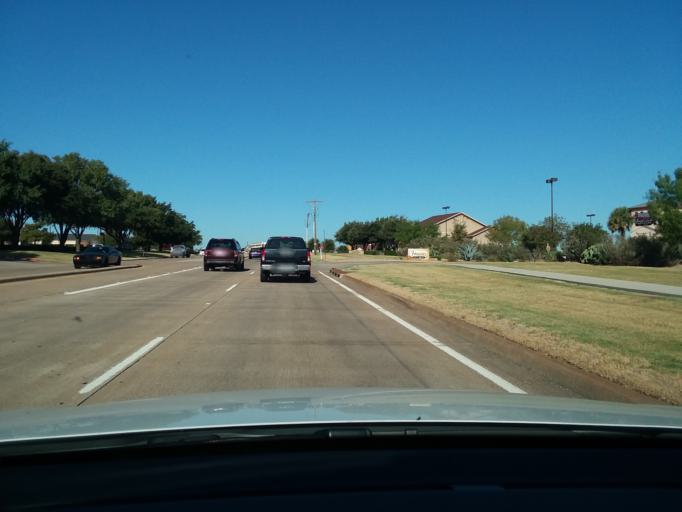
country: US
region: Texas
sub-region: Denton County
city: Highland Village
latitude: 33.0731
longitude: -97.0635
